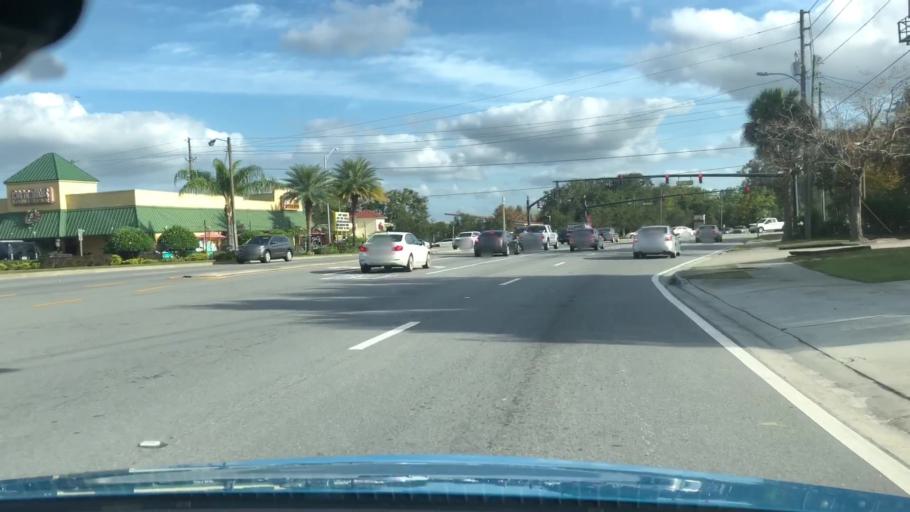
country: US
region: Florida
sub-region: Seminole County
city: Casselberry
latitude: 28.6842
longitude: -81.3352
